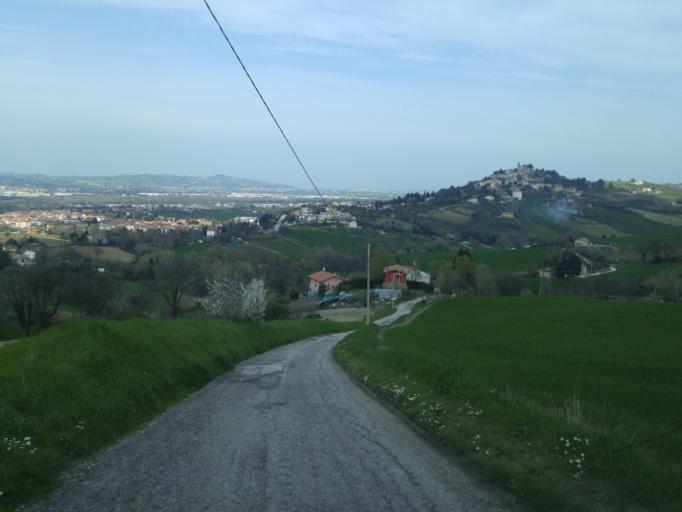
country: IT
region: The Marches
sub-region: Provincia di Pesaro e Urbino
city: Villanova
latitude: 43.7265
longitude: 12.9327
